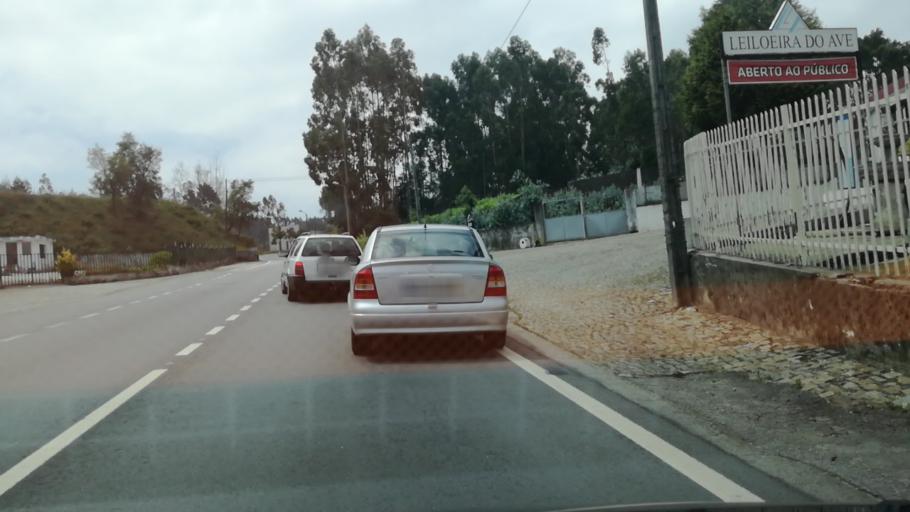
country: PT
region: Porto
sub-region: Trofa
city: Sao Romao do Coronado
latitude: 41.3085
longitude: -8.5814
